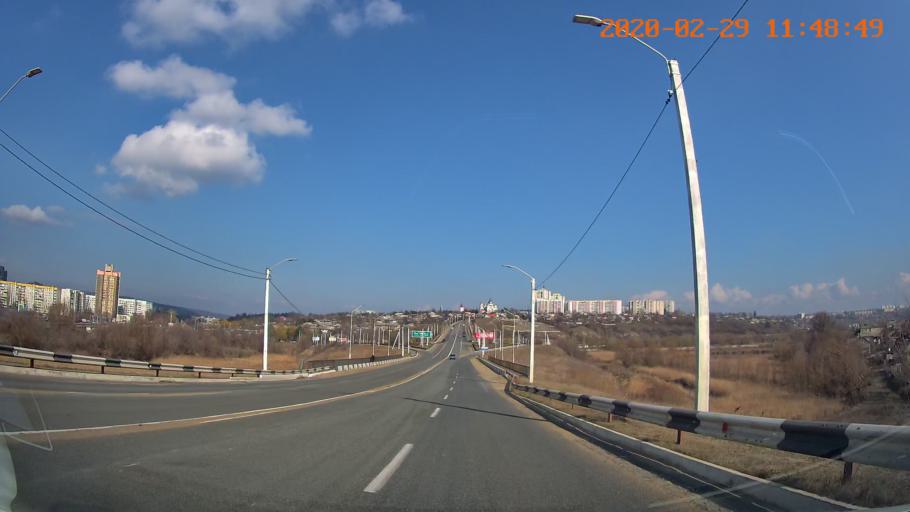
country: MD
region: Telenesti
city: Ribnita
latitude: 47.7505
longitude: 28.9925
